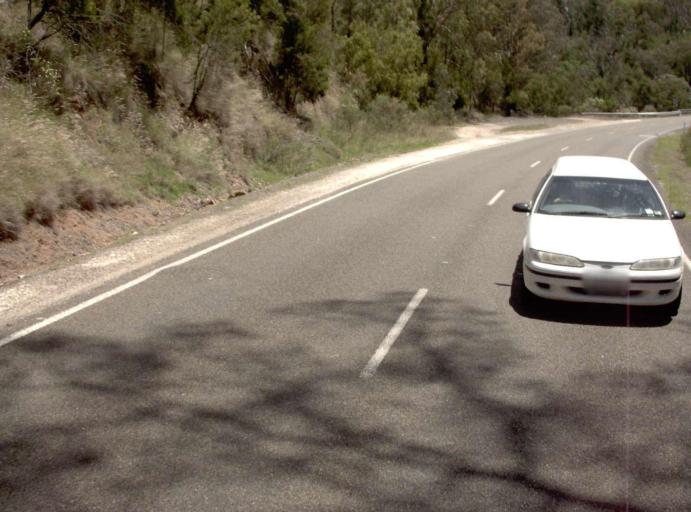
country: AU
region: Victoria
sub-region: East Gippsland
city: Bairnsdale
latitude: -37.4832
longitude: 147.8307
